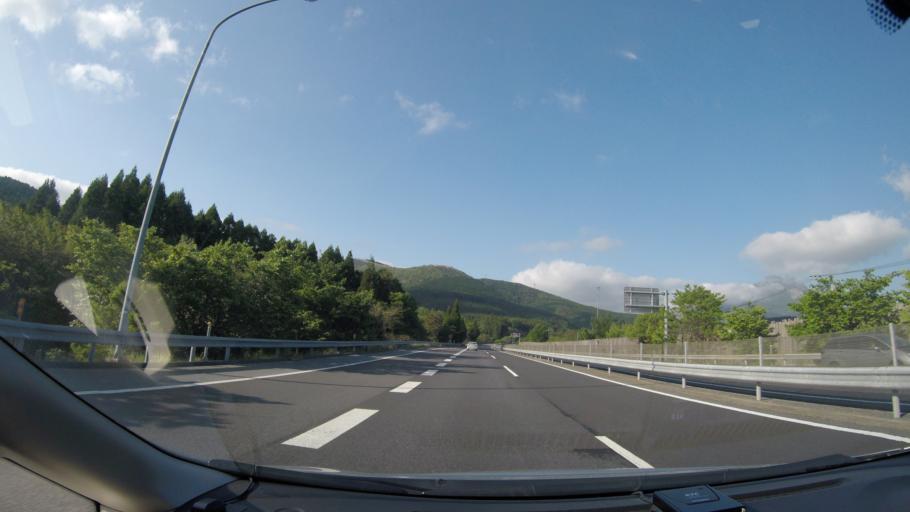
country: JP
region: Oita
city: Beppu
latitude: 33.2599
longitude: 131.3310
